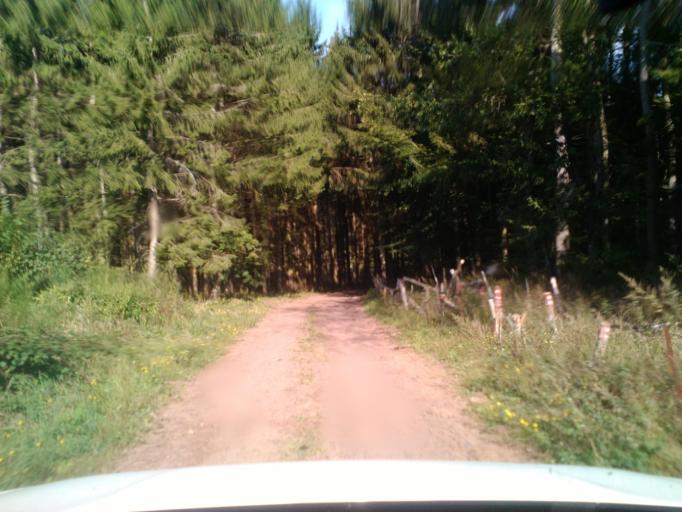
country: FR
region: Lorraine
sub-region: Departement des Vosges
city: Senones
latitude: 48.3589
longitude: 6.9951
